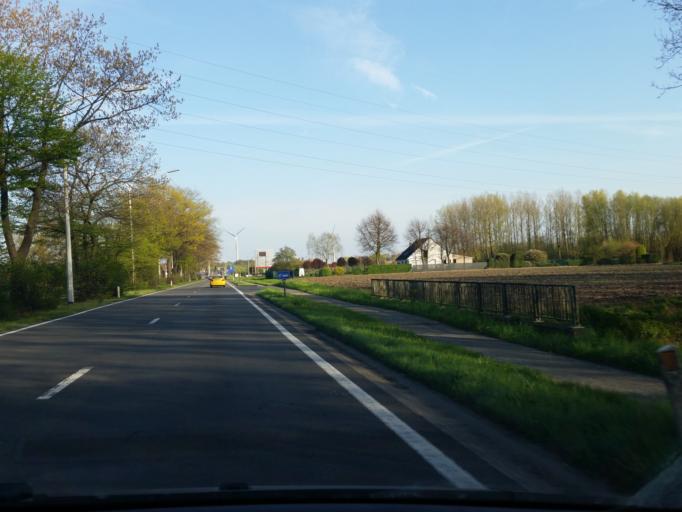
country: BE
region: Flanders
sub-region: Provincie Antwerpen
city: Puurs
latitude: 51.0813
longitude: 4.2909
